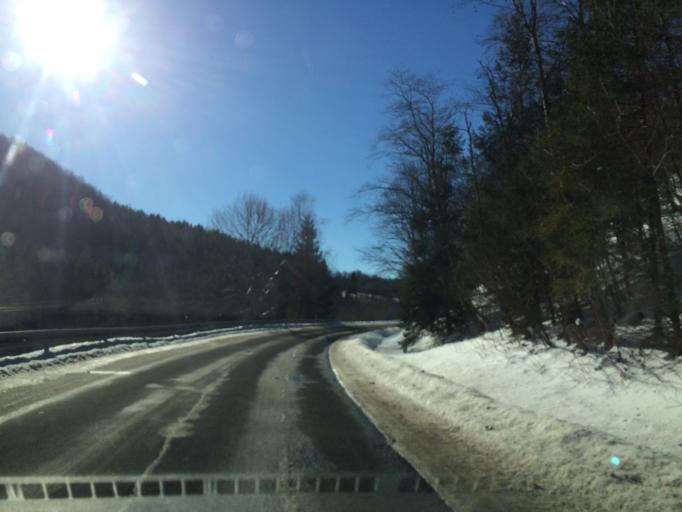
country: PL
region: Subcarpathian Voivodeship
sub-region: Powiat bieszczadzki
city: Lutowiska
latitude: 49.1160
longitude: 22.6631
